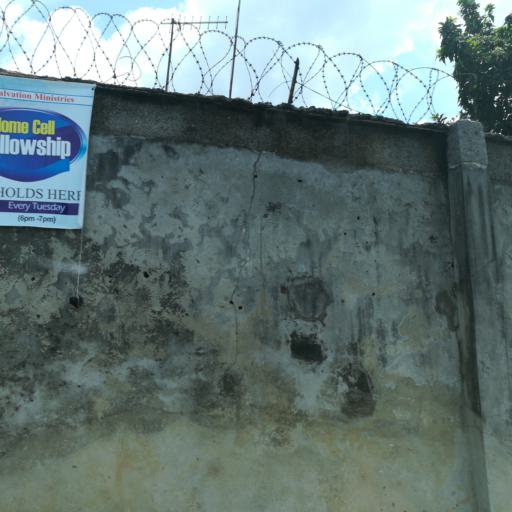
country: NG
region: Rivers
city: Port Harcourt
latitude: 4.7826
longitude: 7.0377
